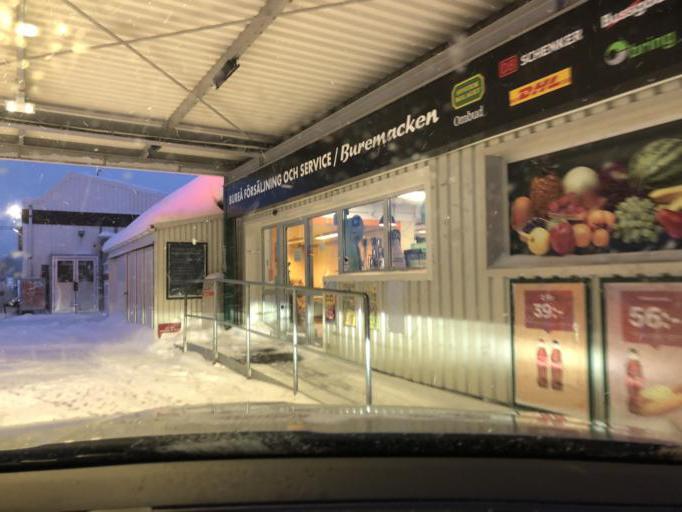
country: SE
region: Vaesterbotten
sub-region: Skelleftea Kommun
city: Burea
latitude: 64.6178
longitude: 21.1993
